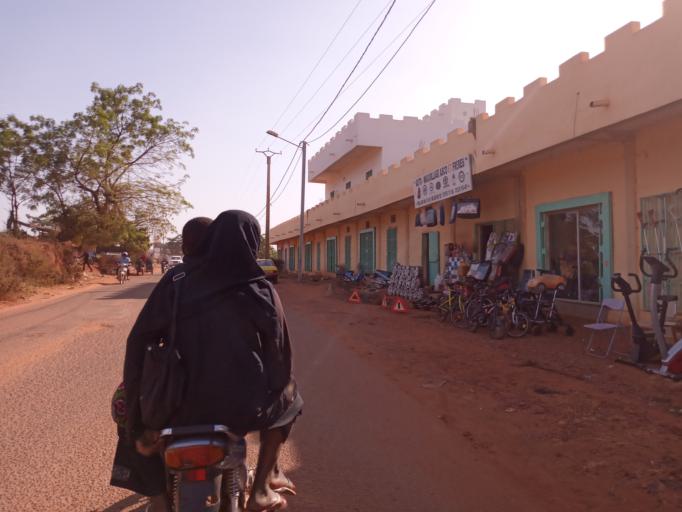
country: ML
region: Bamako
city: Bamako
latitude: 12.6261
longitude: -7.9553
